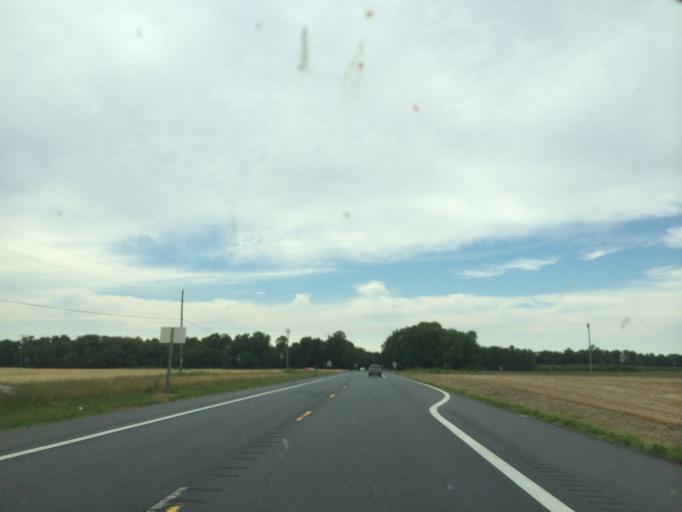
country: US
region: Maryland
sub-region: Caroline County
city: Federalsburg
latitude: 38.8028
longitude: -75.7257
